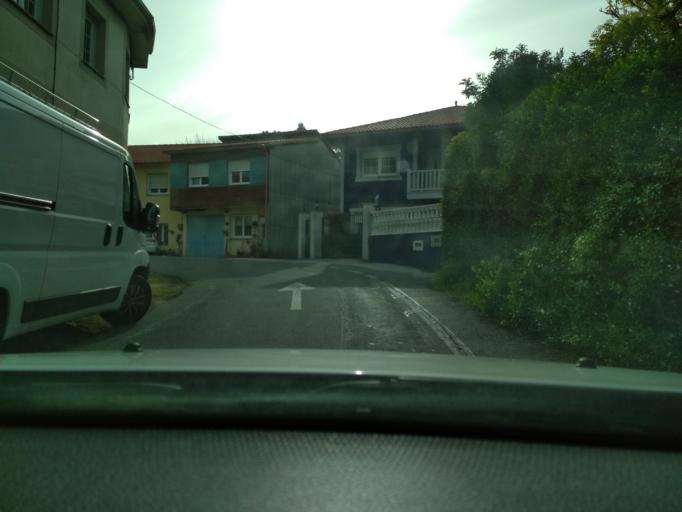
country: ES
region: Galicia
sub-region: Provincia da Coruna
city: Culleredo
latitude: 43.2874
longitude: -8.3902
